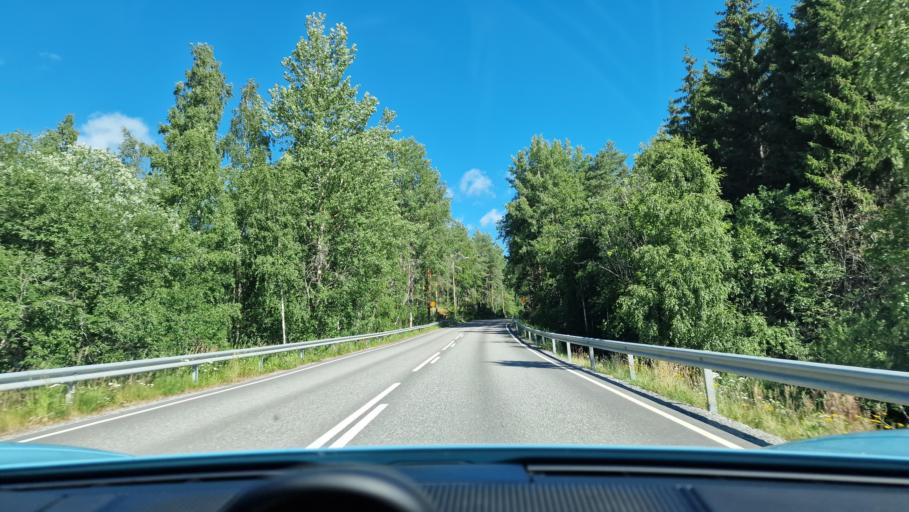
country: FI
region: Pirkanmaa
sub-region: Tampere
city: Orivesi
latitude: 61.6048
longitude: 24.3101
